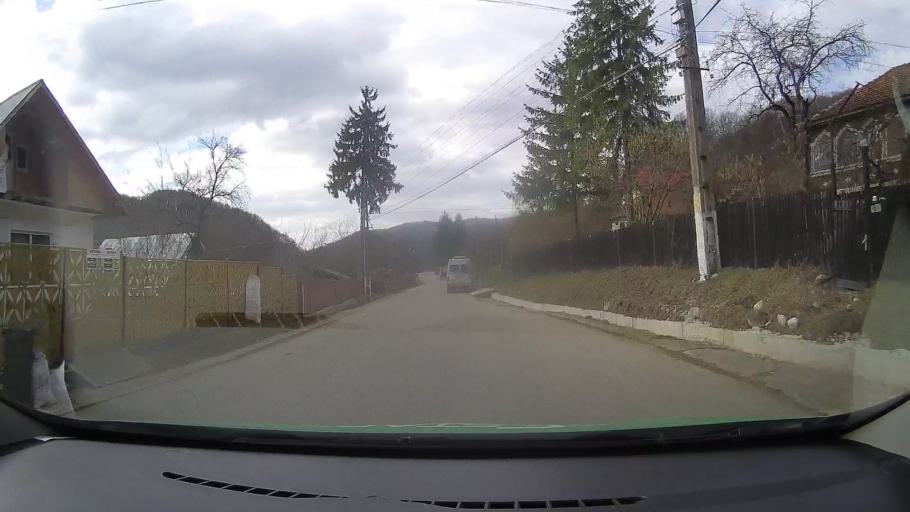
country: RO
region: Dambovita
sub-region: Comuna Visinesti
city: Visinesti
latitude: 45.1024
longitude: 25.5811
